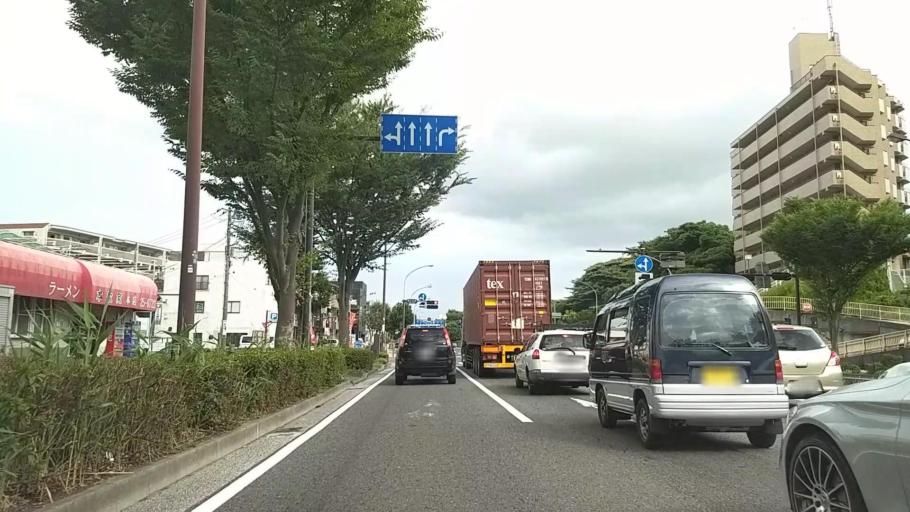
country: JP
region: Kanagawa
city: Yokohama
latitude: 35.4080
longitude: 139.5647
